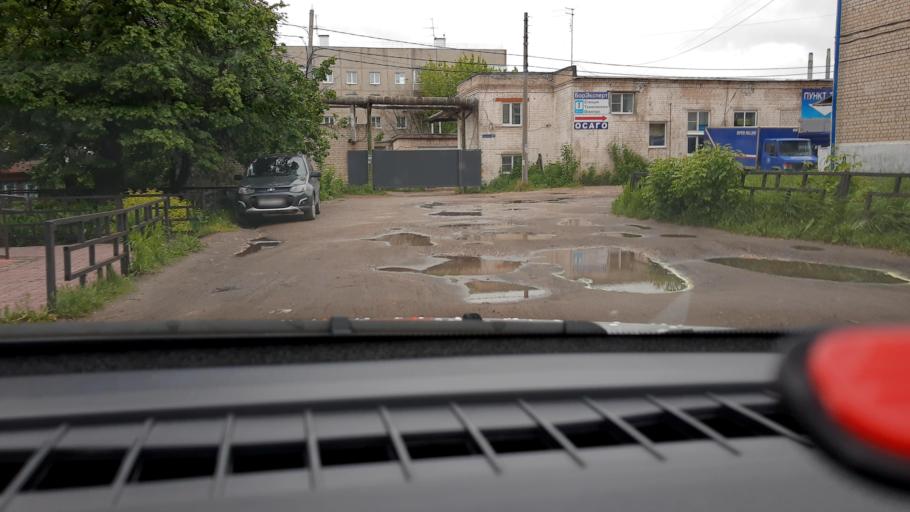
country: RU
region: Nizjnij Novgorod
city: Bor
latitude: 56.3624
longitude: 44.0616
